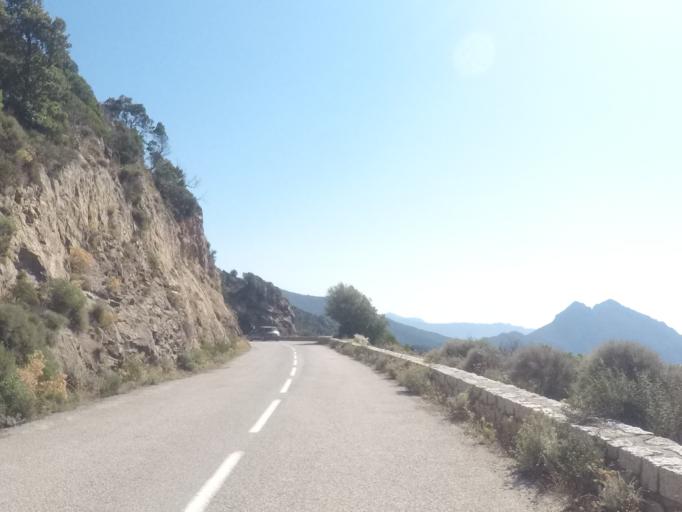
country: FR
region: Corsica
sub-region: Departement de la Haute-Corse
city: Calvi
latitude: 42.3633
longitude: 8.6483
